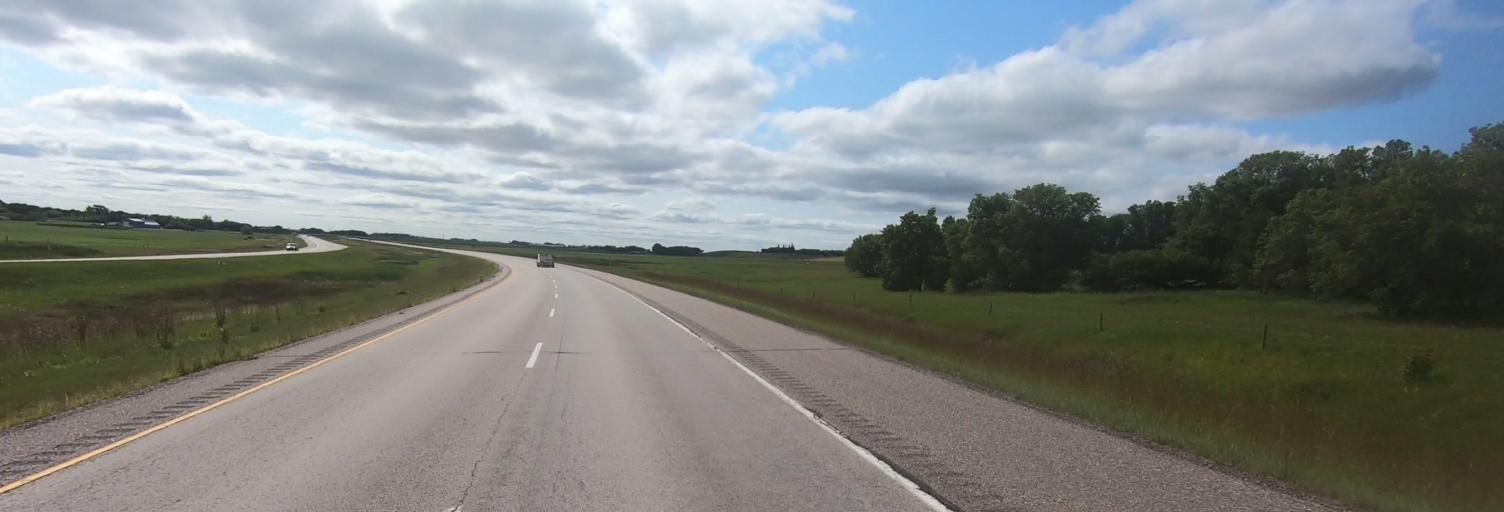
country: CA
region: Manitoba
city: Rivers
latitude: 49.8367
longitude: -100.2924
